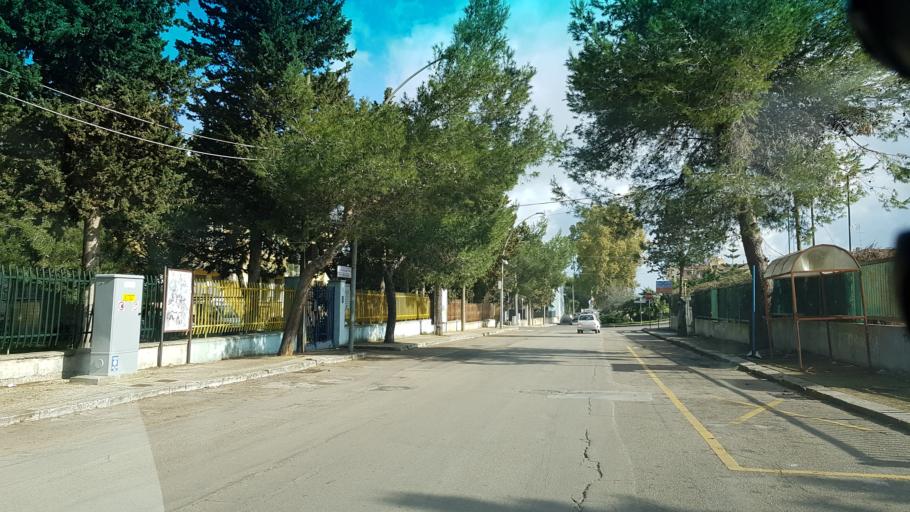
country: IT
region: Apulia
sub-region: Provincia di Brindisi
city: San Pietro Vernotico
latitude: 40.4812
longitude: 18.0015
